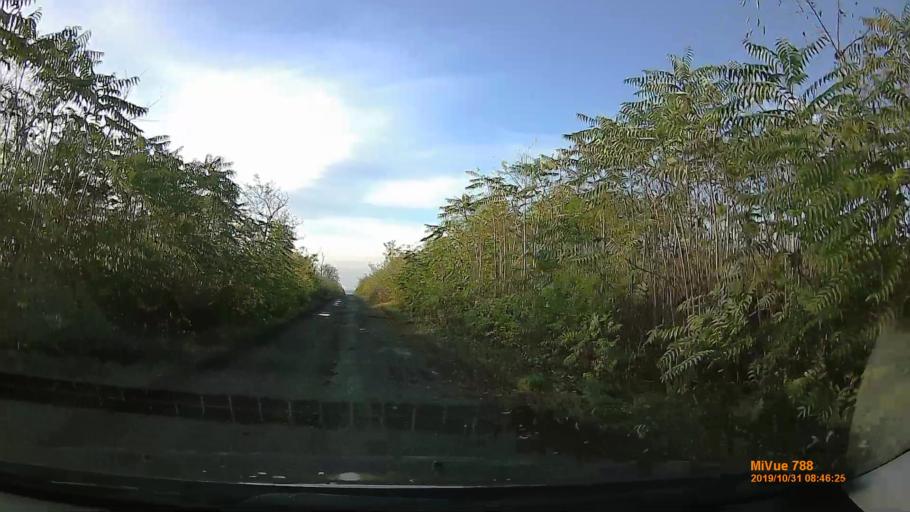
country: HU
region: Pest
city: Albertirsa
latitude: 47.2850
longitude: 19.6108
